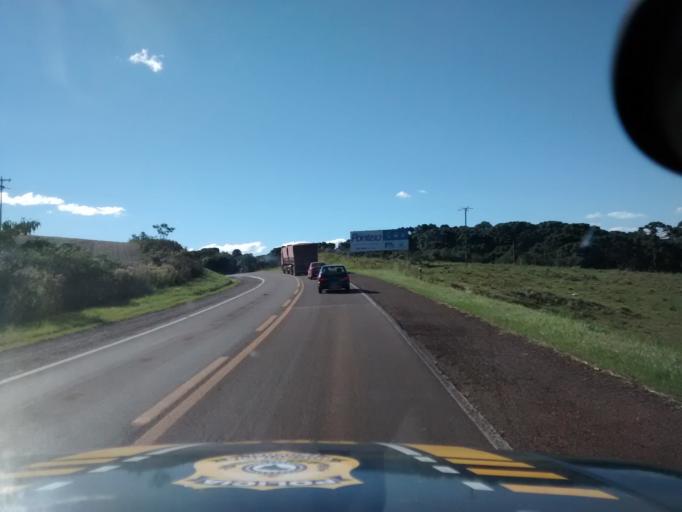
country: BR
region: Rio Grande do Sul
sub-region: Lagoa Vermelha
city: Lagoa Vermelha
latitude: -28.2890
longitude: -51.4633
